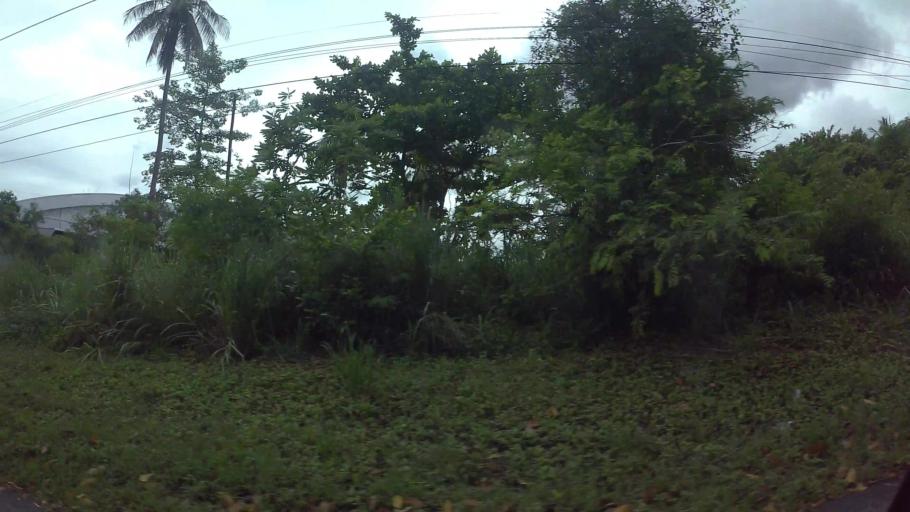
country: TH
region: Chon Buri
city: Si Racha
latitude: 13.1895
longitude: 100.9956
